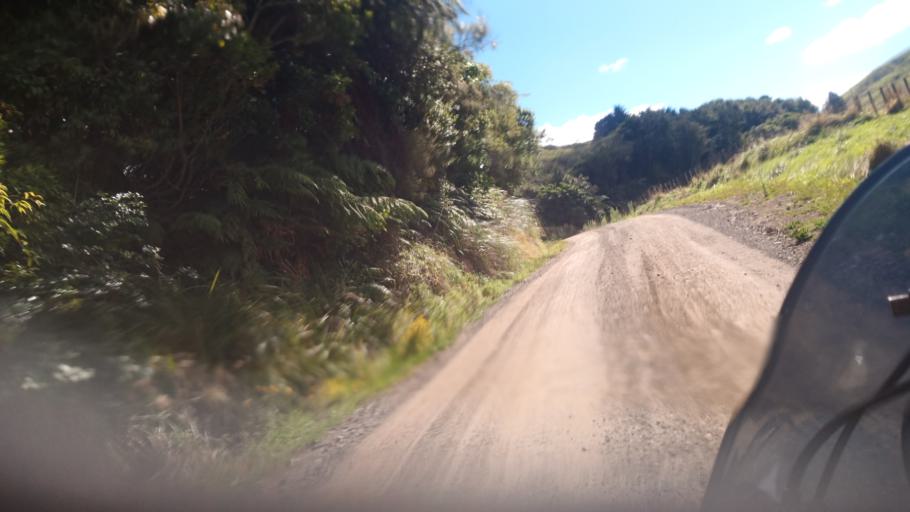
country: NZ
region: Bay of Plenty
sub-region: Opotiki District
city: Opotiki
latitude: -38.3426
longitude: 177.5821
